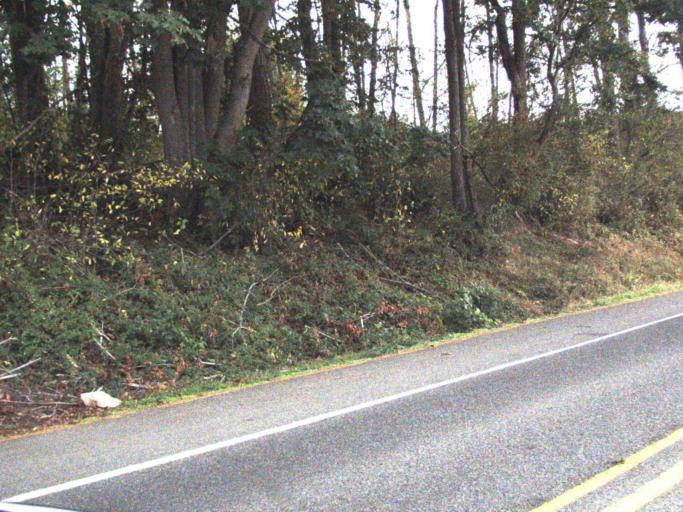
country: US
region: Washington
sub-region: Jefferson County
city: Port Hadlock-Irondale
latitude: 48.0518
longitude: -122.8195
